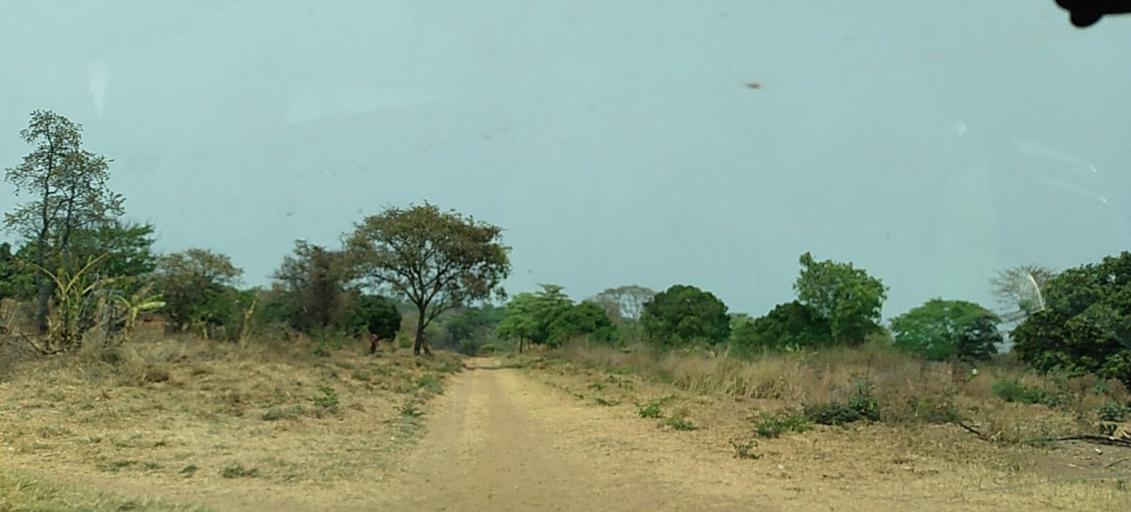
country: ZM
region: Western
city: Lukulu
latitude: -13.9800
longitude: 23.2285
